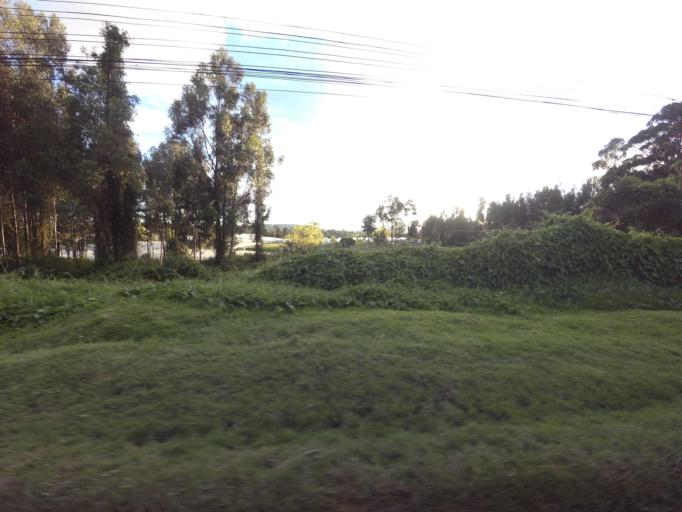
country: CO
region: Cundinamarca
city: Cota
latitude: 4.7826
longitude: -74.0274
